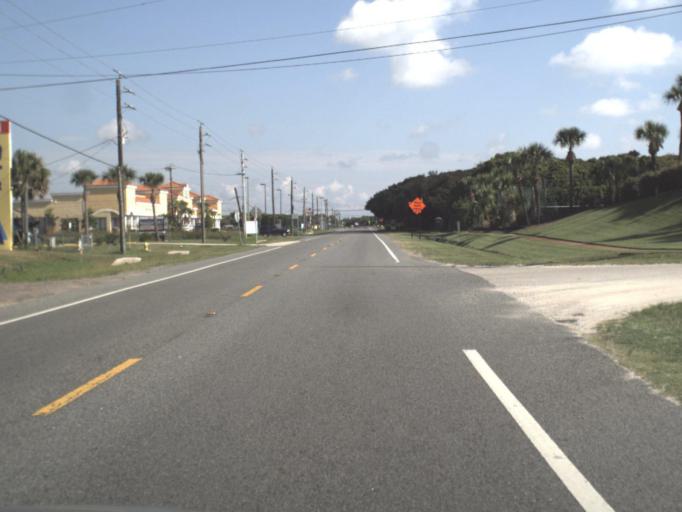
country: US
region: Florida
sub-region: Saint Johns County
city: Butler Beach
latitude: 29.7888
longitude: -81.2602
